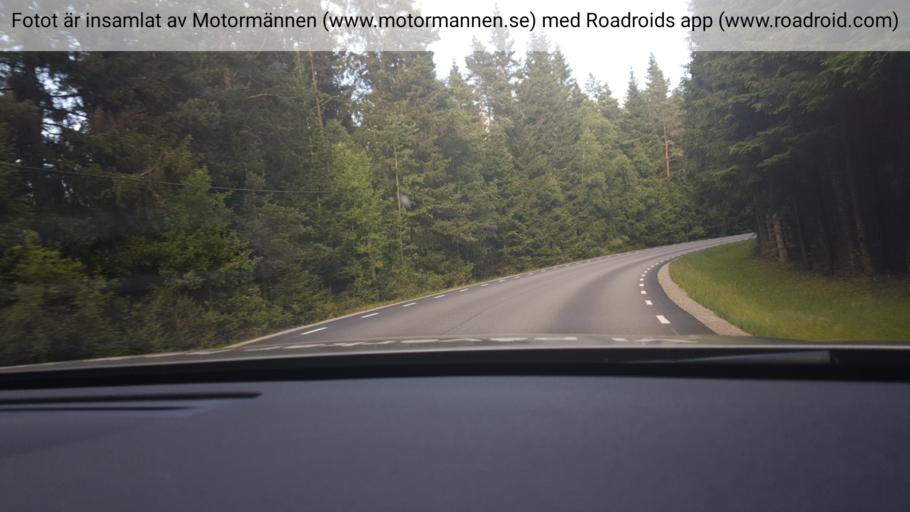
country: SE
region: Joenkoeping
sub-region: Gnosjo Kommun
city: Gnosjoe
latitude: 57.5664
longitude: 13.6042
